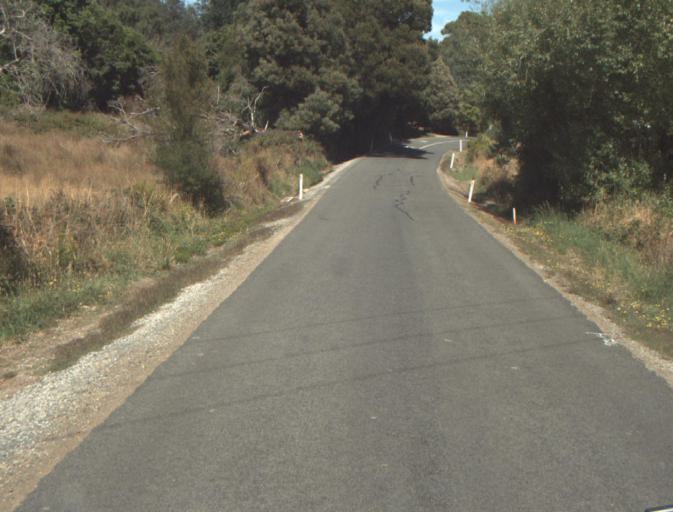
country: AU
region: Tasmania
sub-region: Launceston
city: Mayfield
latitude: -41.2587
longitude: 147.1807
